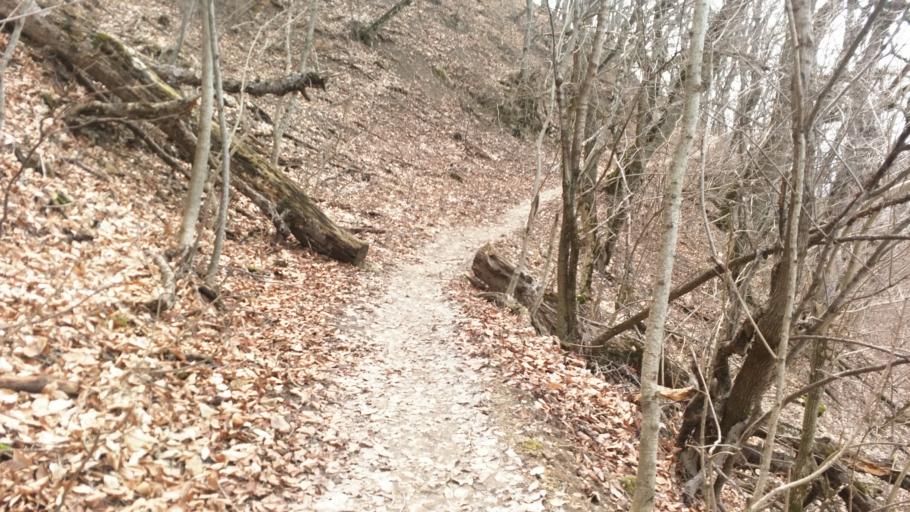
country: RU
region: Stavropol'skiy
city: Zheleznovodsk
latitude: 44.1395
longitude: 43.0273
